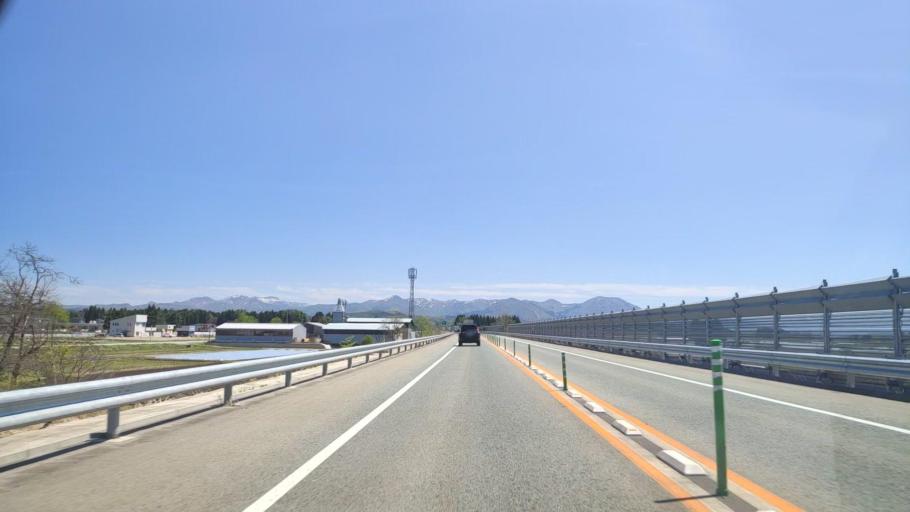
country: JP
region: Yamagata
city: Obanazawa
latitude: 38.6267
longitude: 140.3764
